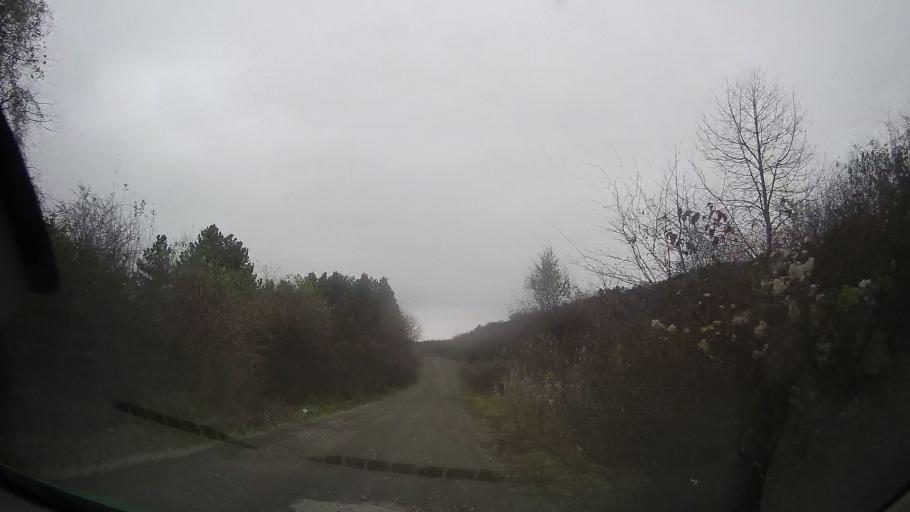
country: RO
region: Mures
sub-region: Comuna Bala
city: Bala
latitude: 46.6806
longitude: 24.4868
